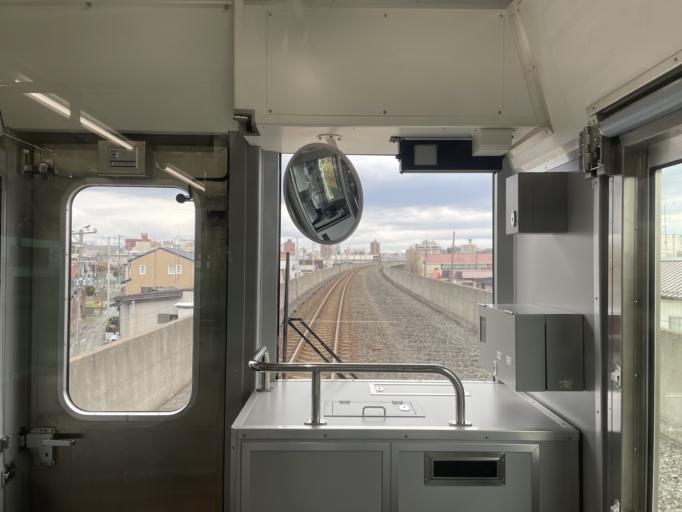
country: JP
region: Aomori
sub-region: Hachinohe Shi
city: Uchimaru
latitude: 40.5177
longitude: 141.5029
